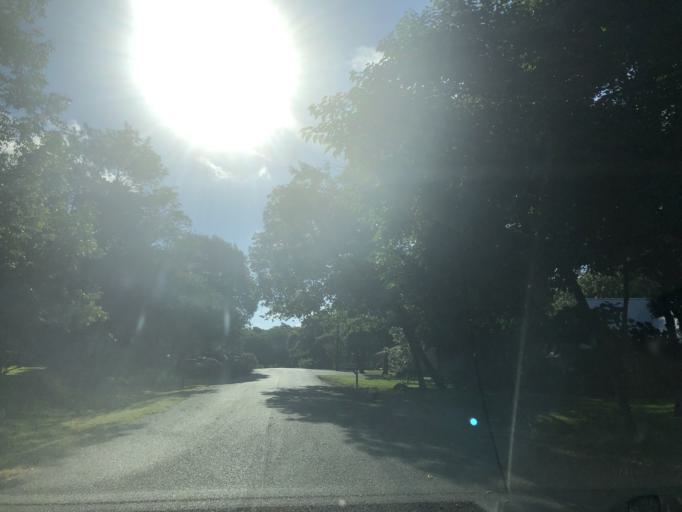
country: US
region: Texas
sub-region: Dallas County
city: Duncanville
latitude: 32.6638
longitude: -96.9217
